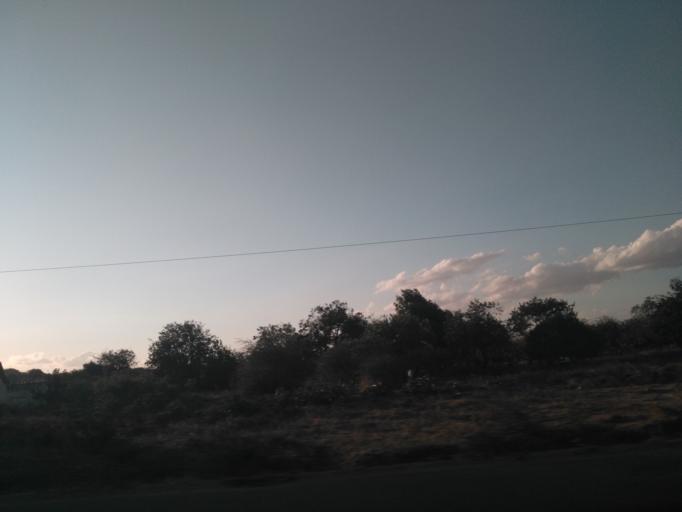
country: TZ
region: Dodoma
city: Dodoma
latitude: -6.1786
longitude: 35.7350
